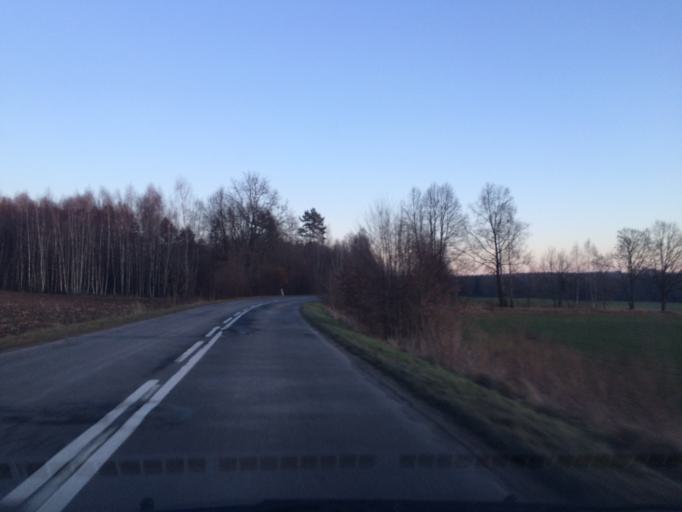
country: PL
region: Lower Silesian Voivodeship
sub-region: Powiat lwowecki
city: Lwowek Slaski
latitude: 51.1191
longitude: 15.6405
